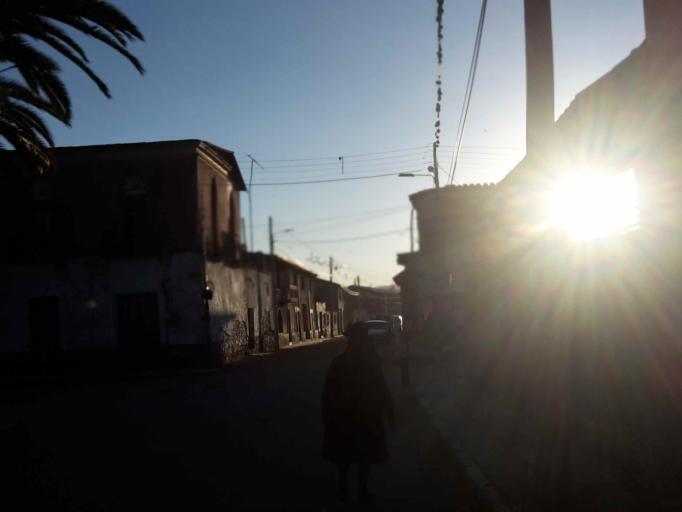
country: BO
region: Cochabamba
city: Capinota
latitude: -17.5499
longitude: -66.2483
